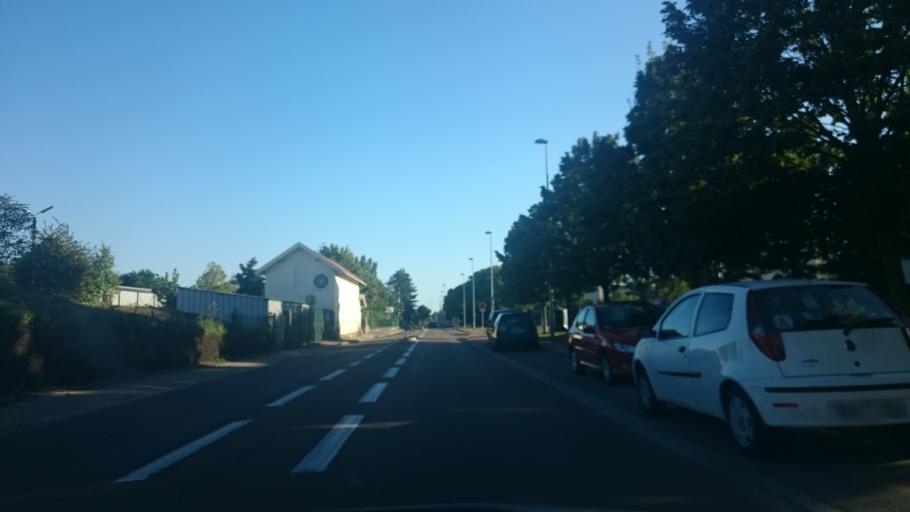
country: FR
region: Bourgogne
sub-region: Departement de la Cote-d'Or
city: Saint-Apollinaire
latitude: 47.3469
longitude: 5.0595
